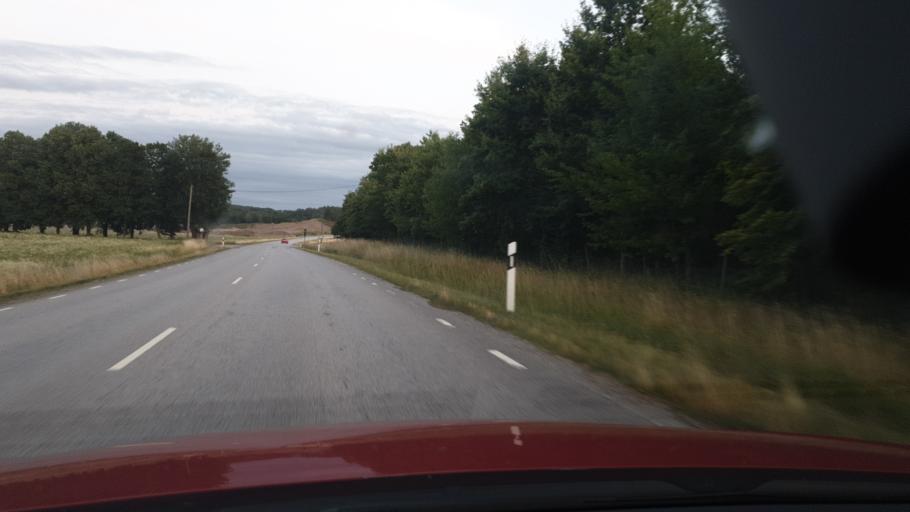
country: SE
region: Uppsala
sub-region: Habo Kommun
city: Balsta
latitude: 59.6185
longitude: 17.4978
